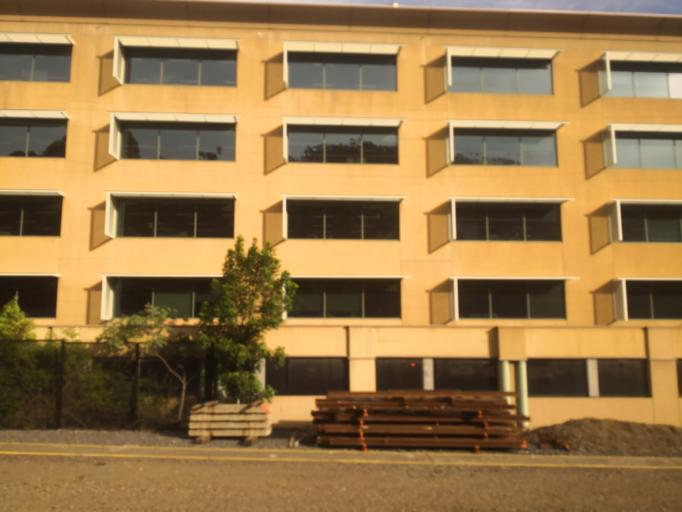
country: AU
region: New South Wales
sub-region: Gosford Shire
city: Gosford
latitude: -33.4260
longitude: 151.3400
